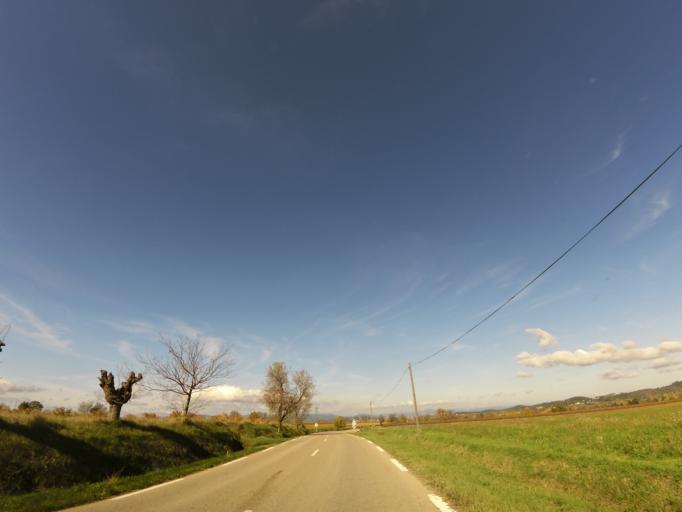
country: FR
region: Languedoc-Roussillon
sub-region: Departement du Gard
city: Ledignan
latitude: 43.9946
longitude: 4.1052
